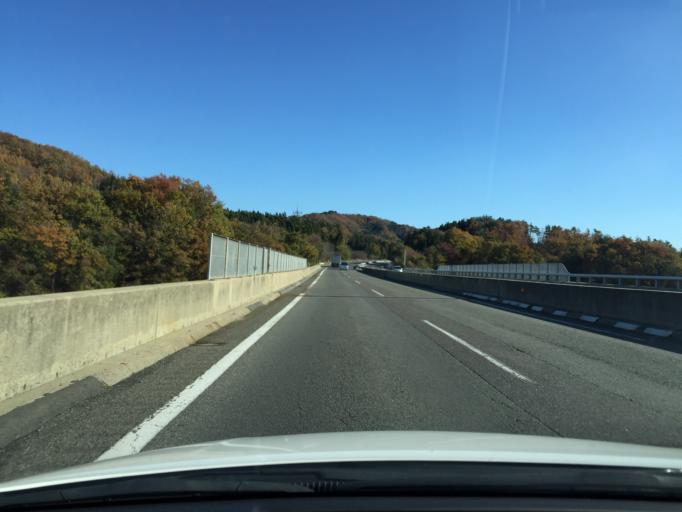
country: JP
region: Fukushima
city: Funehikimachi-funehiki
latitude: 37.4249
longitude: 140.5538
